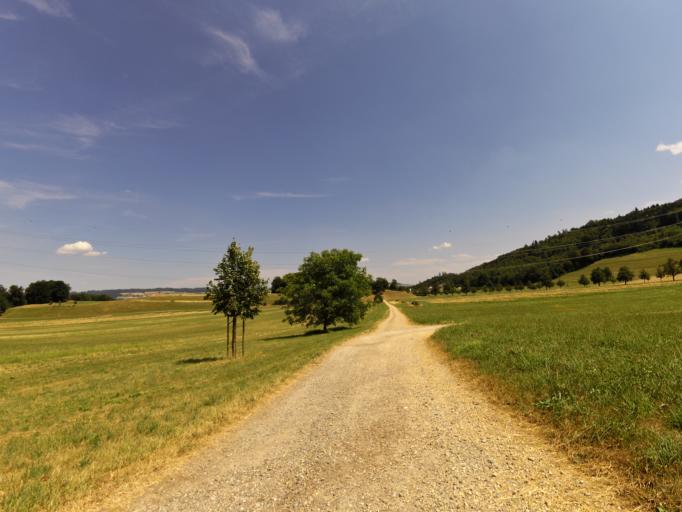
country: CH
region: Aargau
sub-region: Bezirk Bremgarten
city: Hagglingen
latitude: 47.4144
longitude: 8.2435
